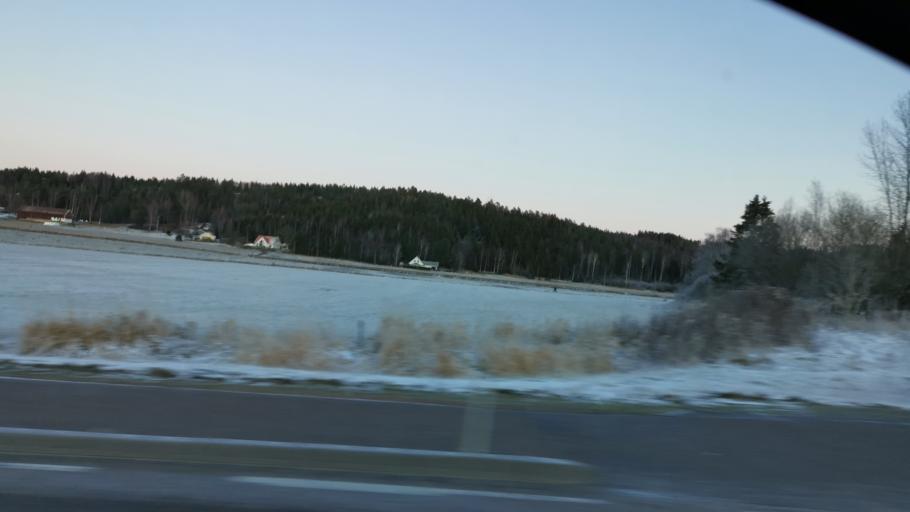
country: SE
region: Vaestra Goetaland
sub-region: Munkedals Kommun
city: Munkedal
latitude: 58.3902
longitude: 11.7625
